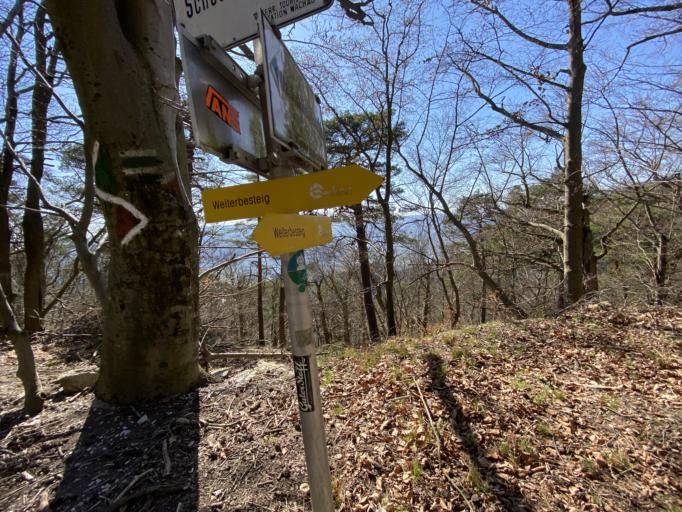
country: AT
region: Lower Austria
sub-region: Politischer Bezirk Krems
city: Durnstein
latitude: 48.4068
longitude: 15.5286
